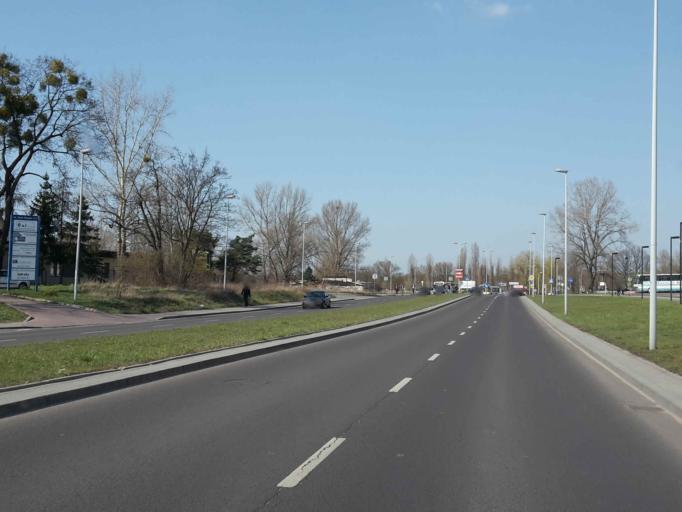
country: PL
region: Kujawsko-Pomorskie
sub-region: Torun
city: Torun
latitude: 53.0151
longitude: 18.5602
